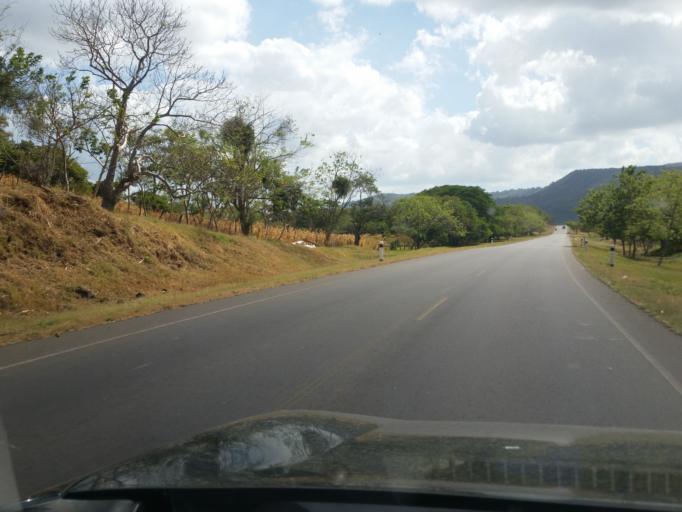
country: NI
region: Chontales
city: Comalapa
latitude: 12.2043
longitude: -85.6273
